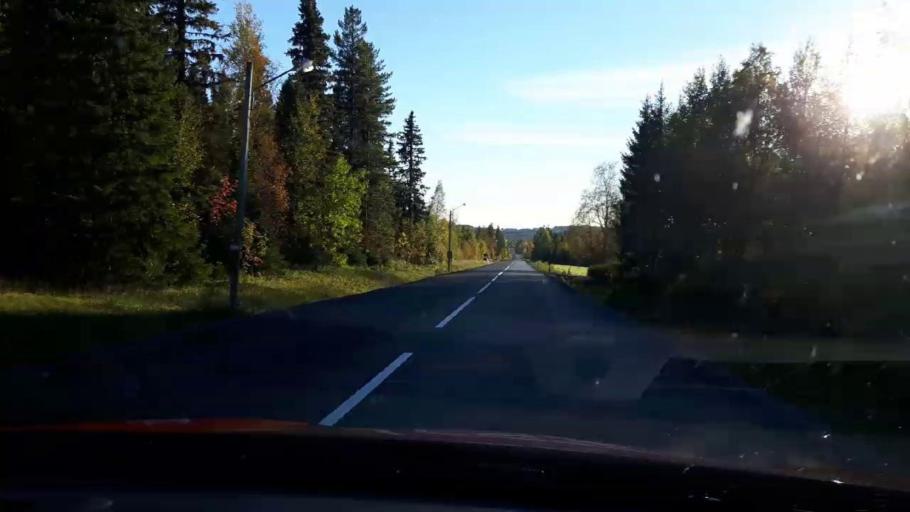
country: SE
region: Jaemtland
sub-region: OEstersunds Kommun
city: Lit
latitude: 63.5618
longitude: 14.9134
